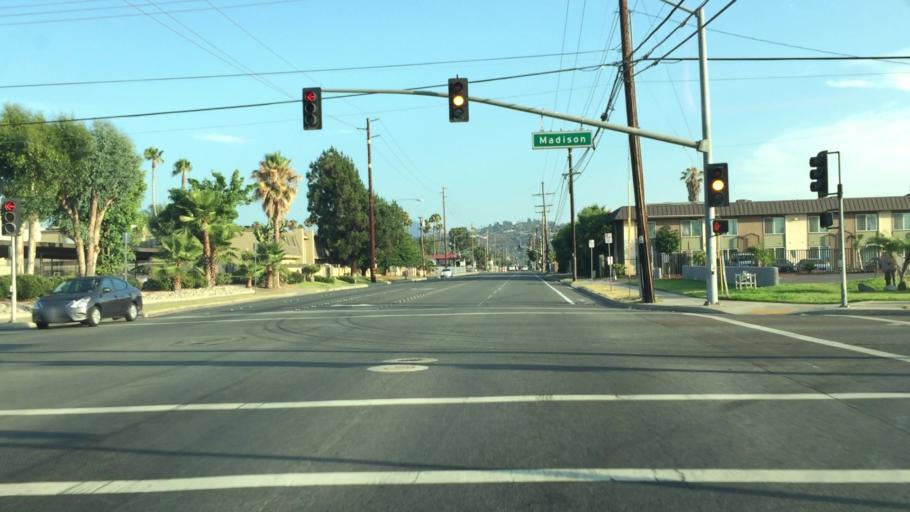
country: US
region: California
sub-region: San Diego County
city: El Cajon
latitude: 32.8003
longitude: -116.9511
